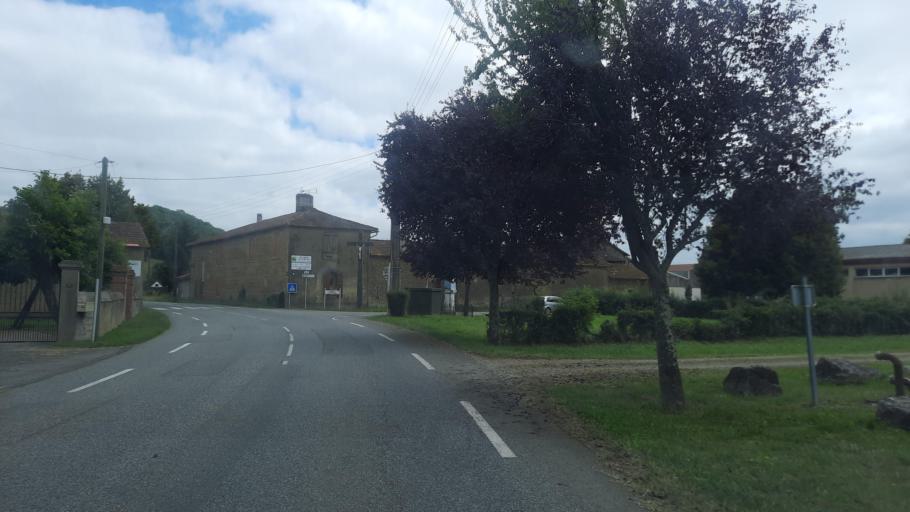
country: FR
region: Midi-Pyrenees
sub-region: Departement des Hautes-Pyrenees
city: Trie-sur-Baise
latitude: 43.3054
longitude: 0.2647
